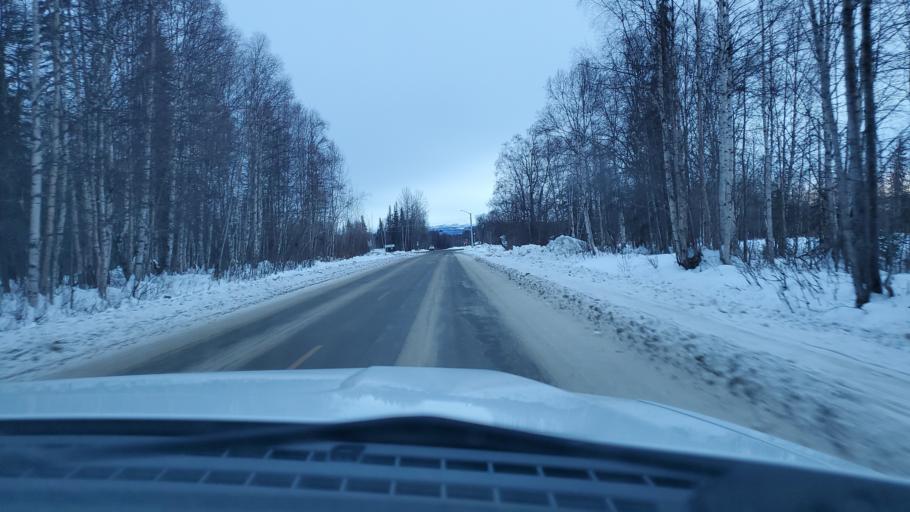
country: US
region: Alaska
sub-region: Matanuska-Susitna Borough
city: Y
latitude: 62.3163
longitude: -150.2382
